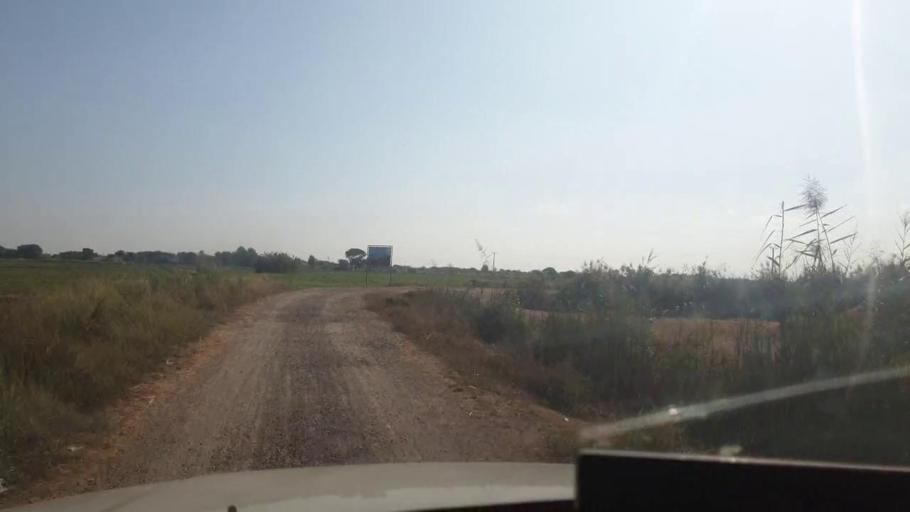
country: PK
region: Sindh
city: Mirpur Sakro
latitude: 24.4665
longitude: 67.5988
